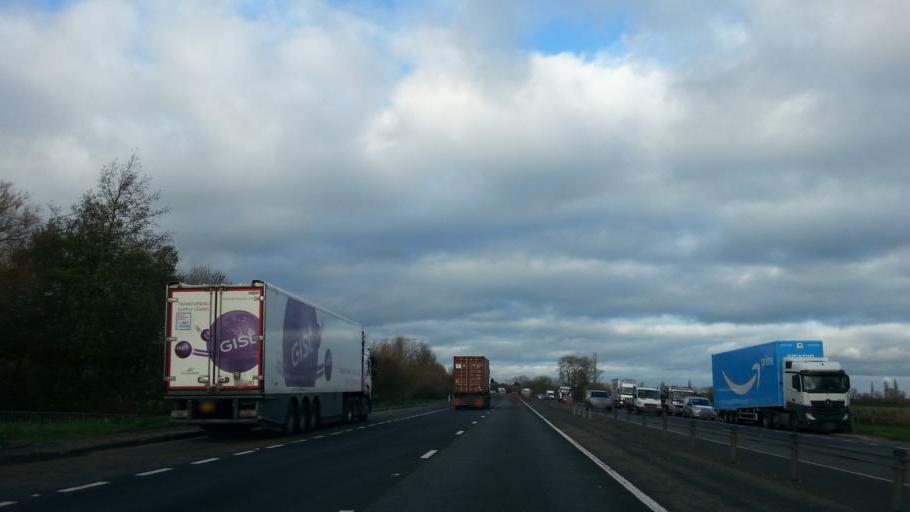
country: GB
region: England
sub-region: Borough of Swindon
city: Wanborough
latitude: 51.5566
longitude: -1.7197
